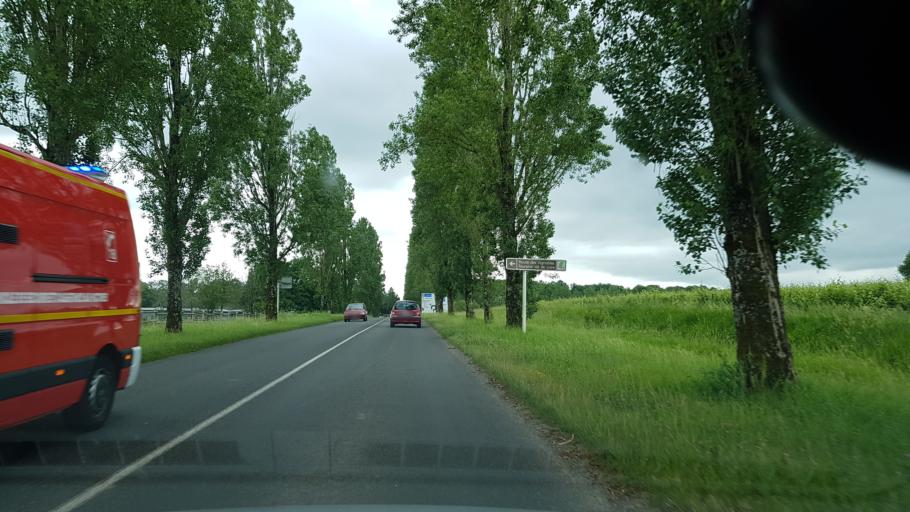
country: FR
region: Centre
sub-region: Departement d'Indre-et-Loire
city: Amboise
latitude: 47.3958
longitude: 0.9795
